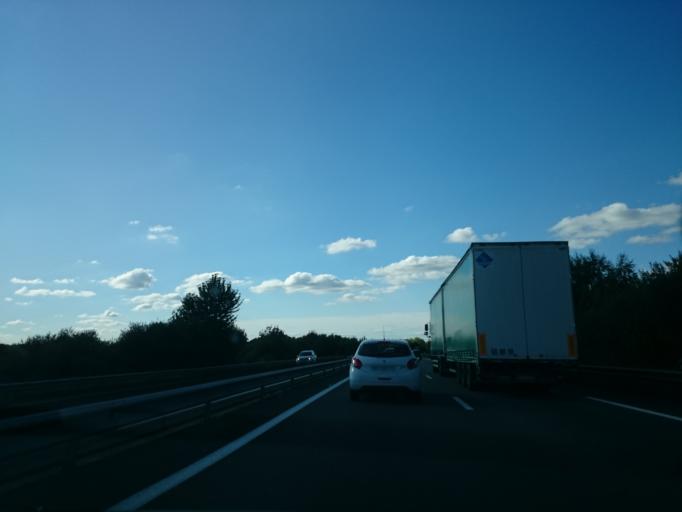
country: FR
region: Pays de la Loire
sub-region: Departement de la Loire-Atlantique
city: Derval
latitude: 47.6549
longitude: -1.6714
